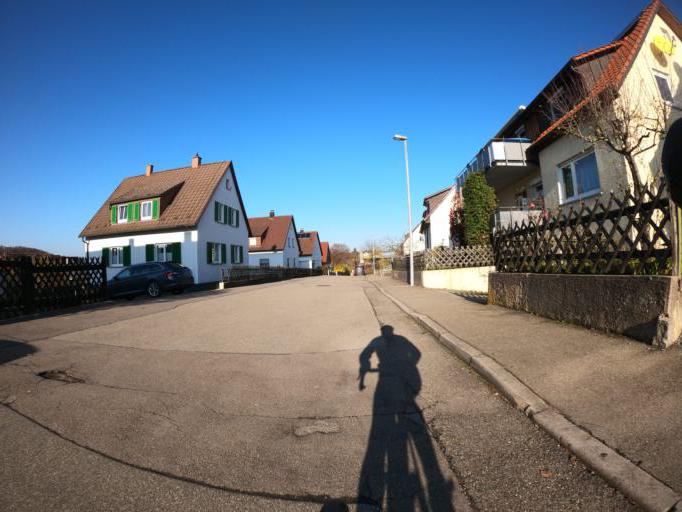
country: DE
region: Baden-Wuerttemberg
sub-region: Regierungsbezirk Stuttgart
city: Aidlingen
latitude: 48.7126
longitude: 8.9131
